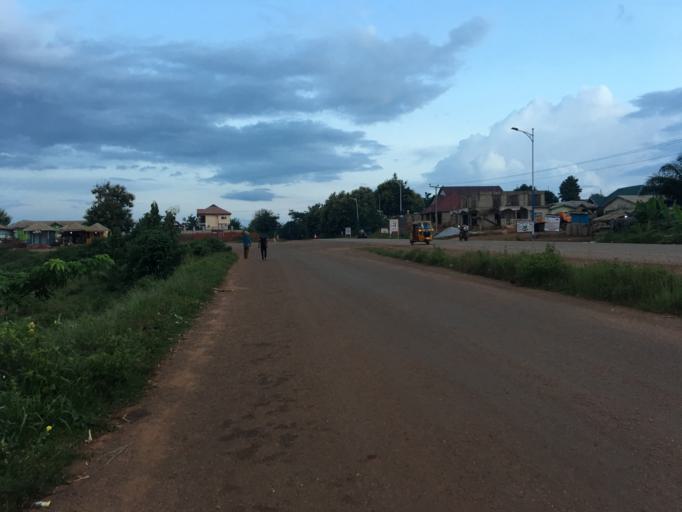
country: GH
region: Western
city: Bibiani
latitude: 6.7882
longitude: -2.5166
